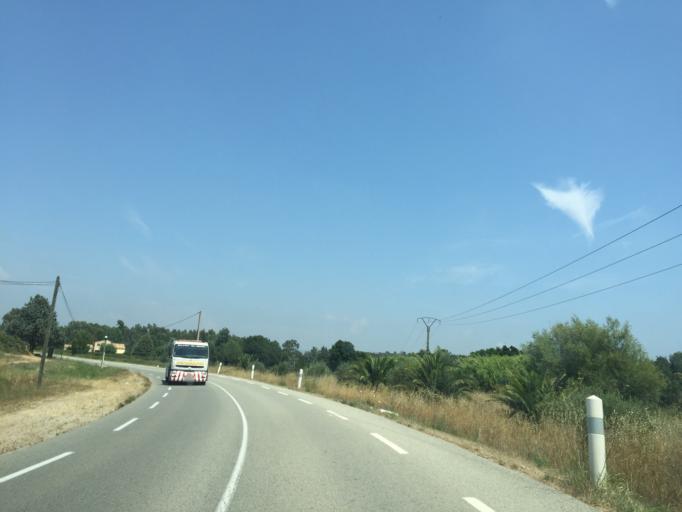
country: FR
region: Provence-Alpes-Cote d'Azur
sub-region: Departement du Var
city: Puget-sur-Argens
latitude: 43.4045
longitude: 6.6845
